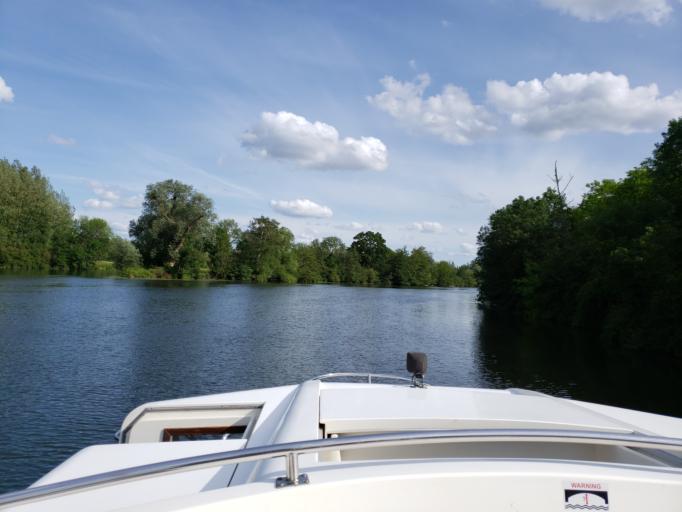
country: FR
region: Bourgogne
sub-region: Departement de l'Yonne
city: Migennes
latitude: 47.9529
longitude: 3.5071
